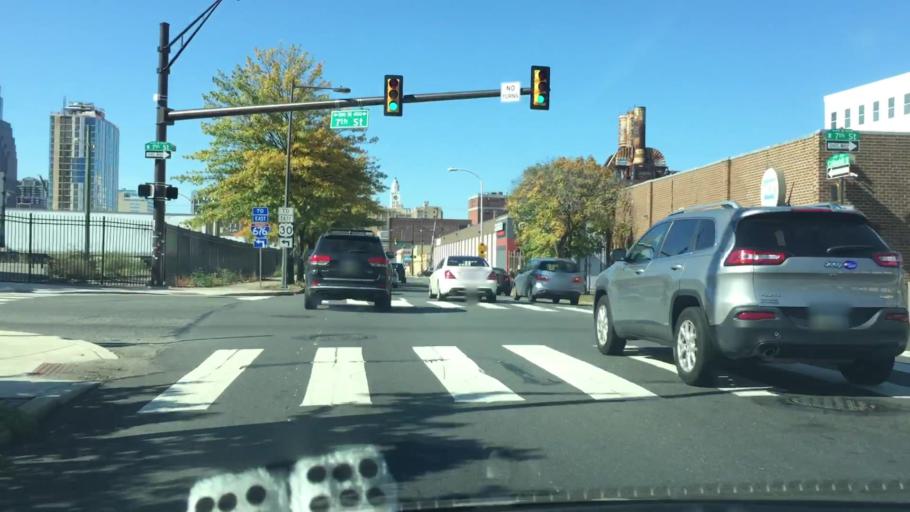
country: US
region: Pennsylvania
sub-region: Philadelphia County
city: Philadelphia
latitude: 39.9581
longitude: -75.1503
